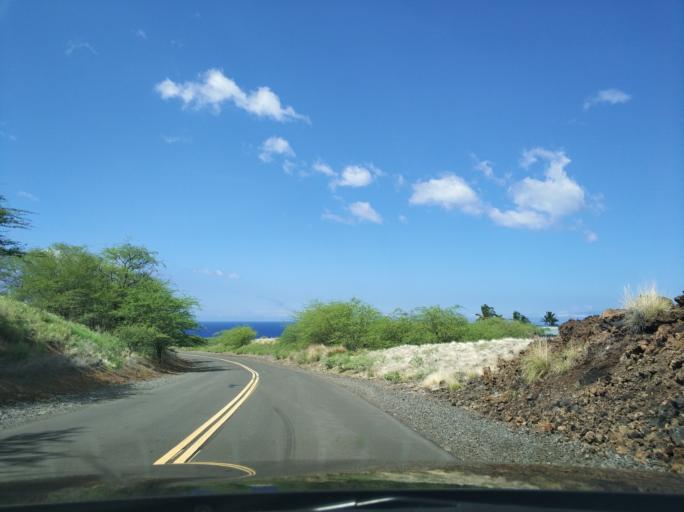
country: US
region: Hawaii
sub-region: Hawaii County
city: Kalaoa
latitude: 19.8010
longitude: -156.0088
